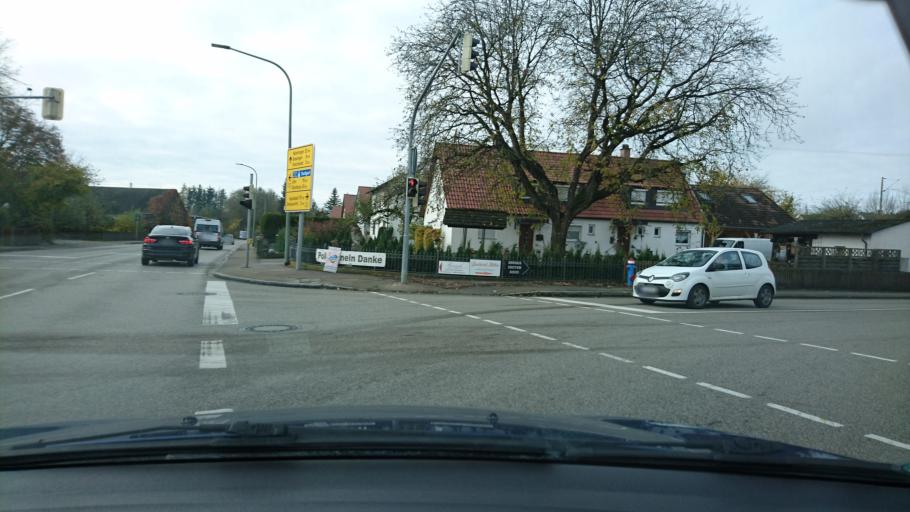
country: DE
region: Bavaria
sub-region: Swabia
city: Tapfheim
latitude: 48.6825
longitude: 10.7087
